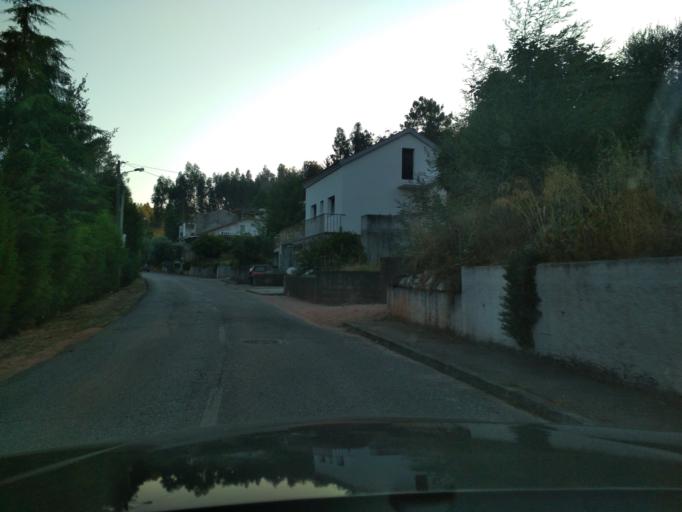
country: PT
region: Coimbra
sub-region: Coimbra
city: Coimbra
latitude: 40.2432
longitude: -8.3980
